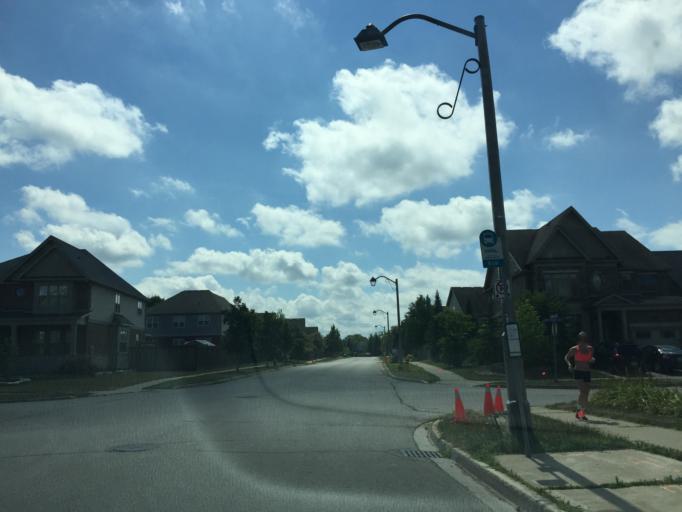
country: CA
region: Ontario
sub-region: Wellington County
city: Guelph
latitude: 43.5177
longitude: -80.1910
